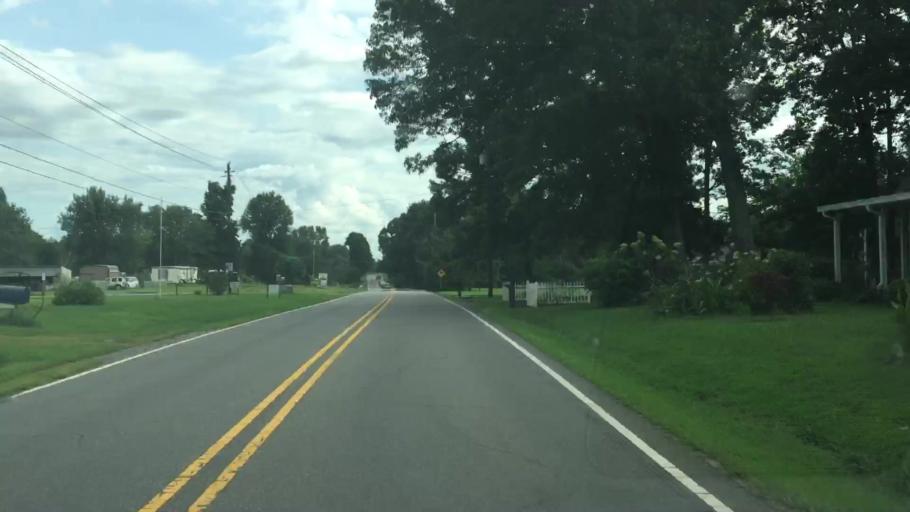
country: US
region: North Carolina
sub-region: Iredell County
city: Mooresville
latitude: 35.6084
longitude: -80.7478
